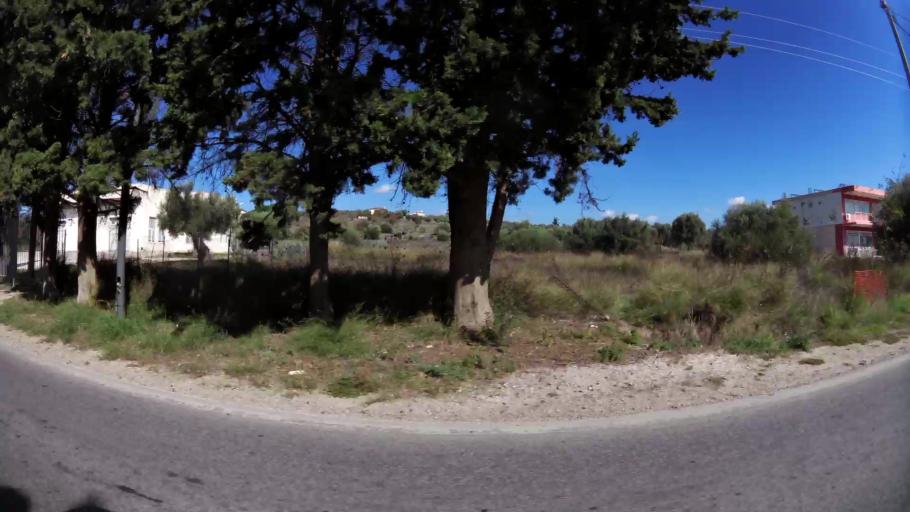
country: GR
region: Attica
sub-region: Nomarchia Anatolikis Attikis
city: Koropi
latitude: 37.8889
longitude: 23.8917
